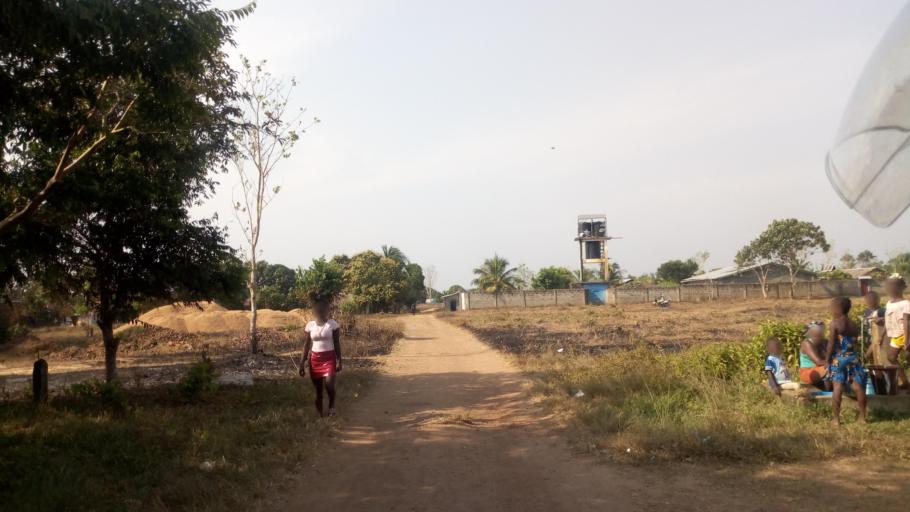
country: SL
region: Southern Province
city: Mogbwemo
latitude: 7.6157
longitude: -12.1797
